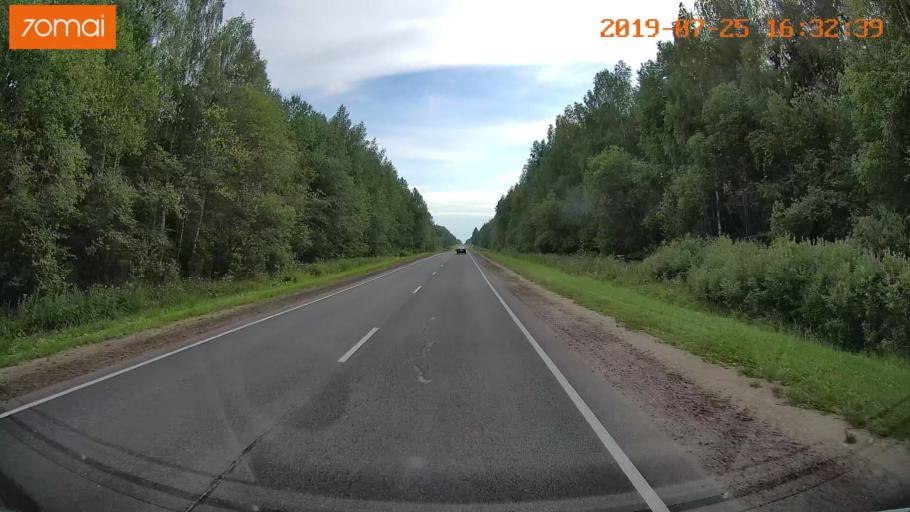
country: RU
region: Ivanovo
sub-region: Privolzhskiy Rayon
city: Ples
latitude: 57.4349
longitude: 41.4710
